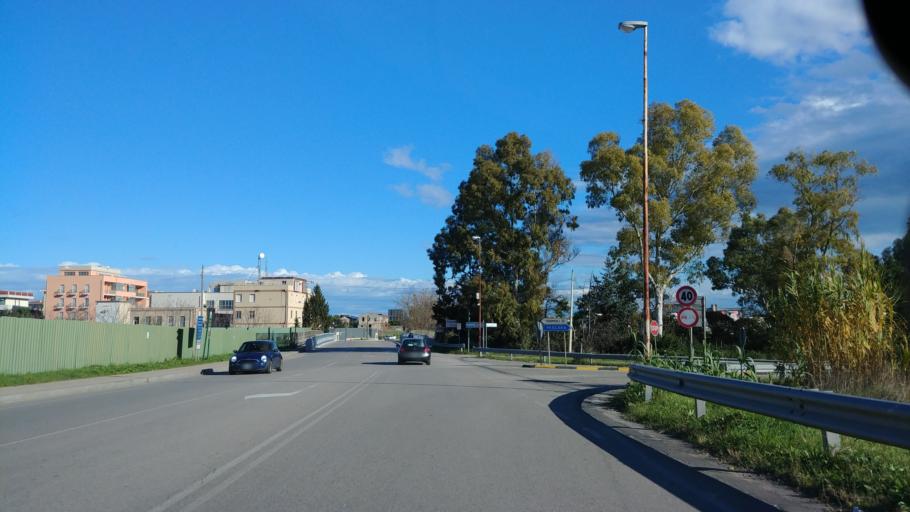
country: IT
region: Molise
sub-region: Provincia di Campobasso
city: Termoli
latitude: 41.9941
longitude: 14.9800
